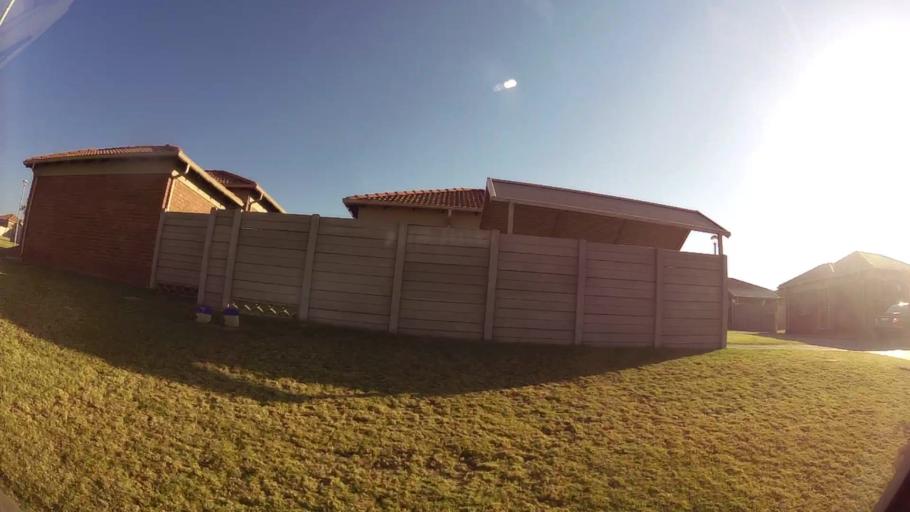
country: ZA
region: Gauteng
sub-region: City of Johannesburg Metropolitan Municipality
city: Midrand
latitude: -25.9080
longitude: 28.1083
